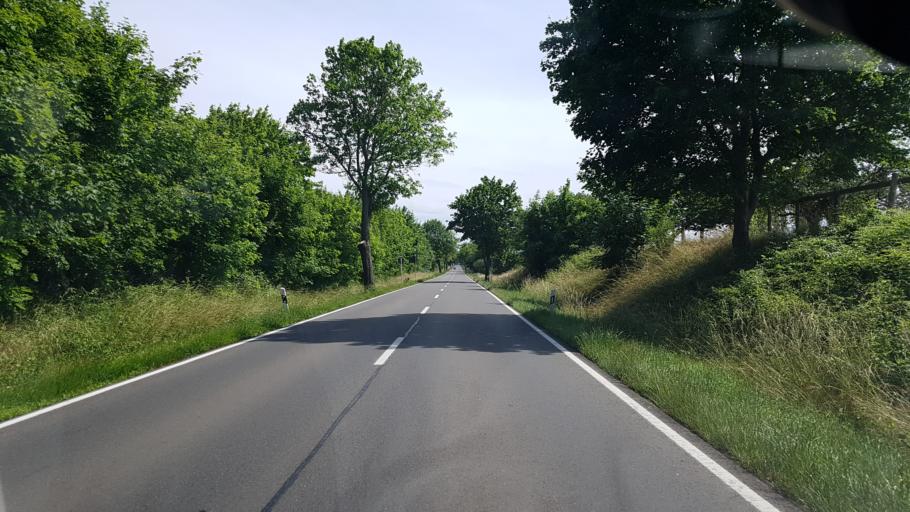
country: DE
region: Brandenburg
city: Prenzlau
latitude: 53.3847
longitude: 13.7771
